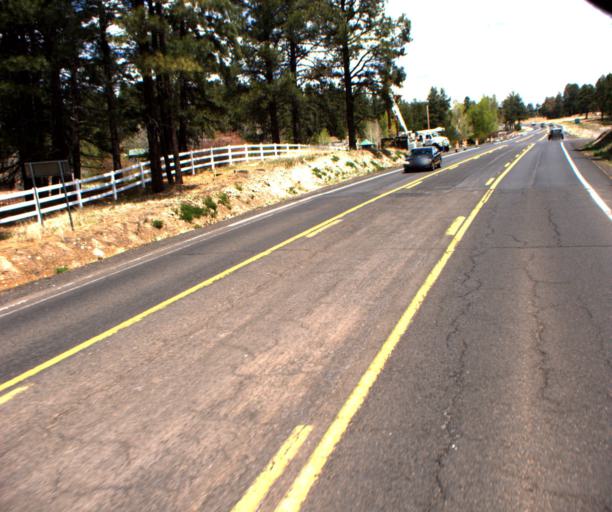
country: US
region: Arizona
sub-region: Coconino County
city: Kachina Village
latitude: 35.1309
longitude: -111.6894
